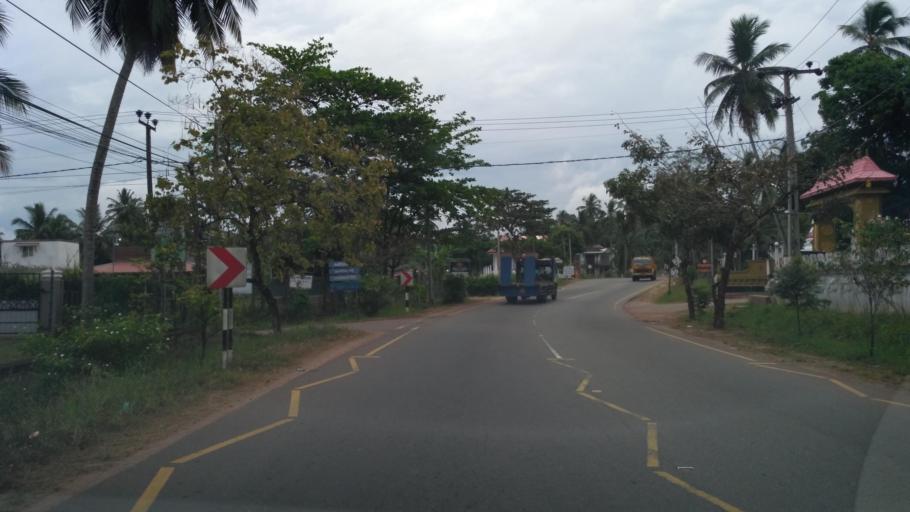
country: LK
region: North Western
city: Kuliyapitiya
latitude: 7.3252
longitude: 80.0377
